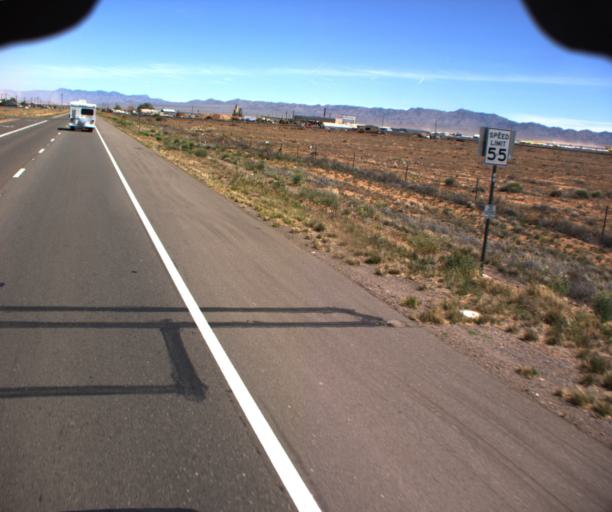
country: US
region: Arizona
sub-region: Mohave County
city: New Kingman-Butler
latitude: 35.2492
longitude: -113.9798
